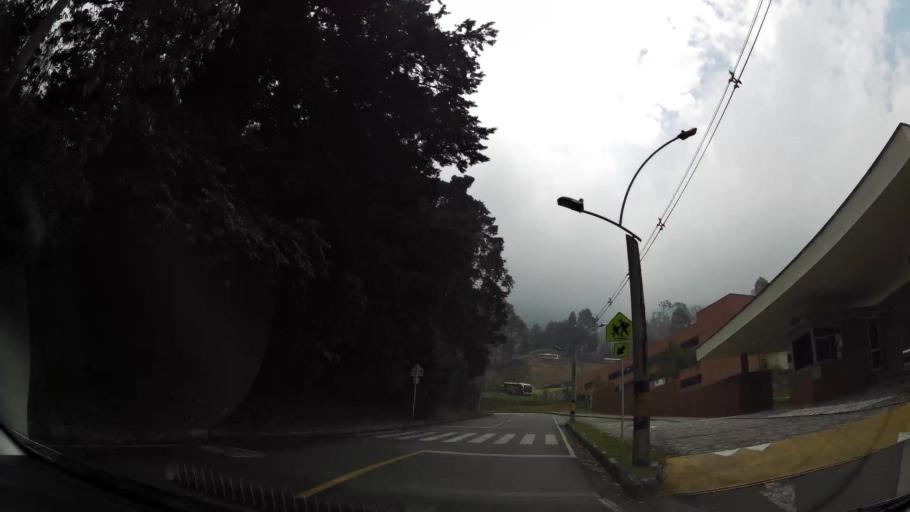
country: CO
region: Antioquia
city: Medellin
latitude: 6.2042
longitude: -75.5466
